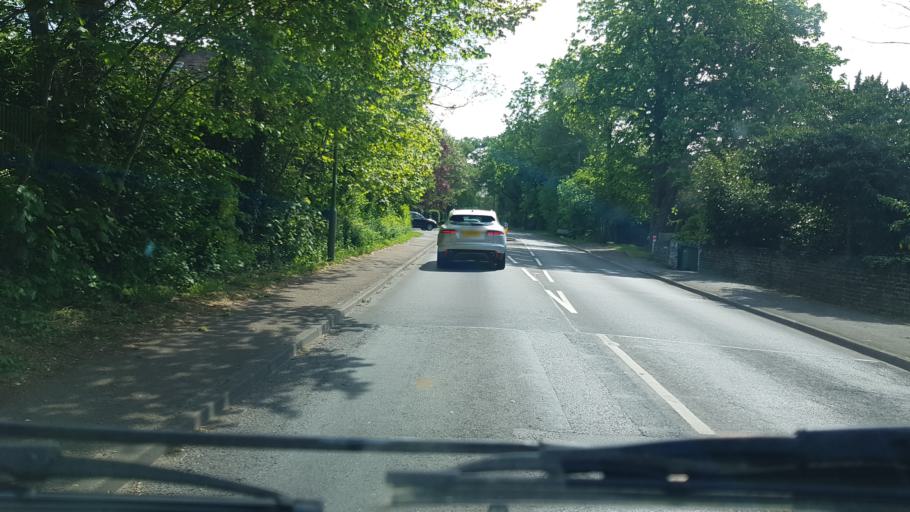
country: GB
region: England
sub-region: Surrey
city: Cobham
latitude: 51.3234
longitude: -0.3918
